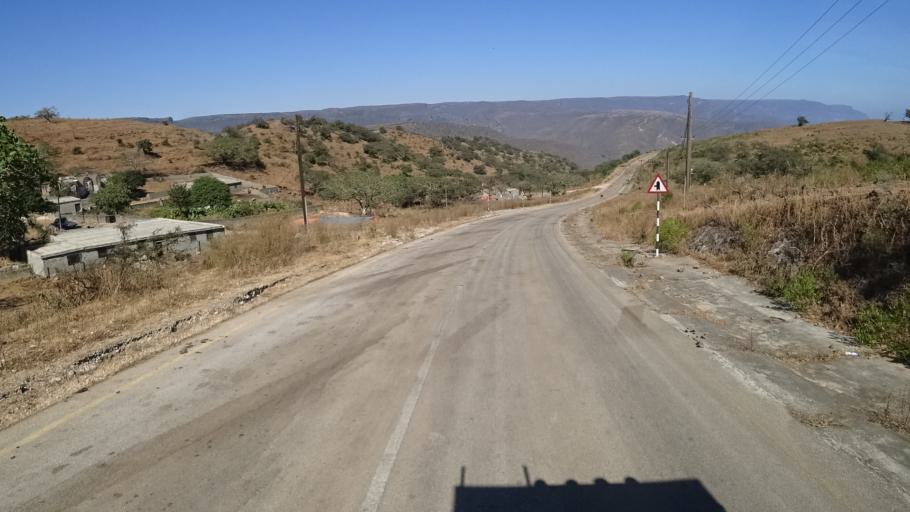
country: YE
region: Al Mahrah
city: Hawf
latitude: 16.7421
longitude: 53.3686
